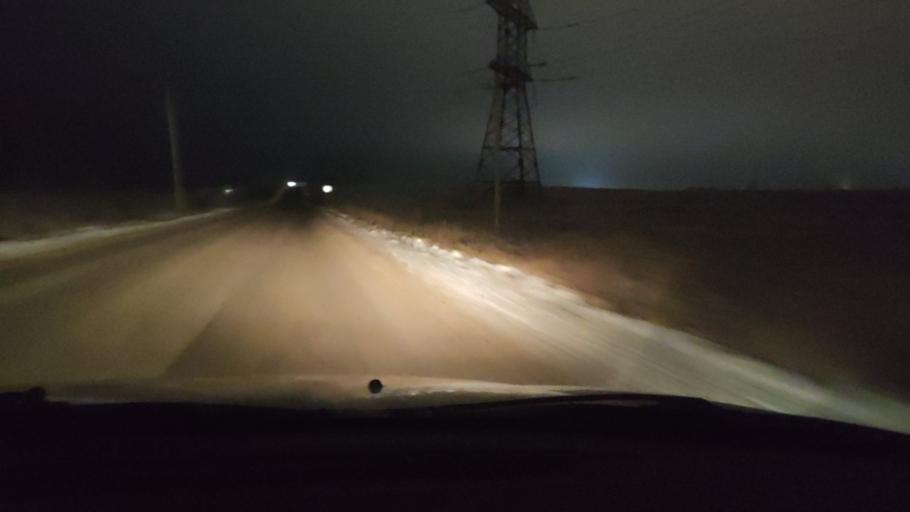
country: RU
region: Perm
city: Ferma
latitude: 57.9173
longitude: 56.3059
